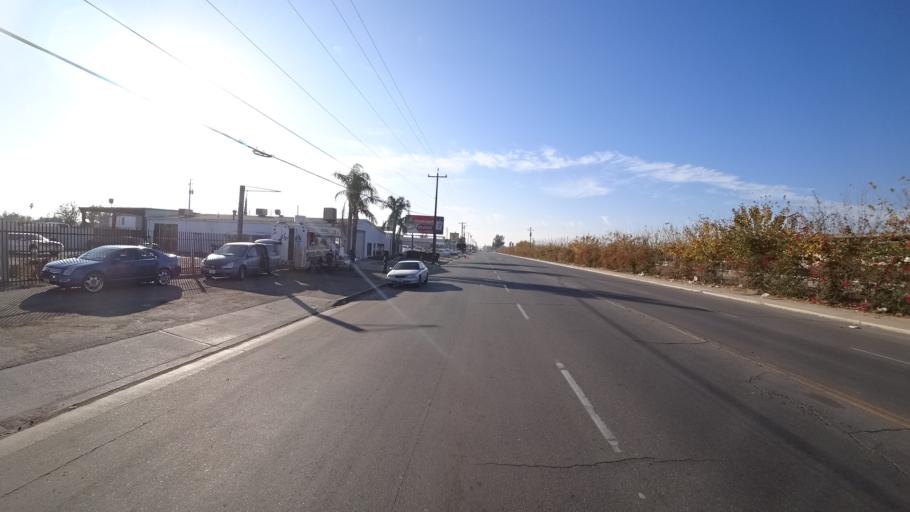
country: US
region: California
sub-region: Kern County
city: Bakersfield
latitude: 35.3394
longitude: -119.0061
